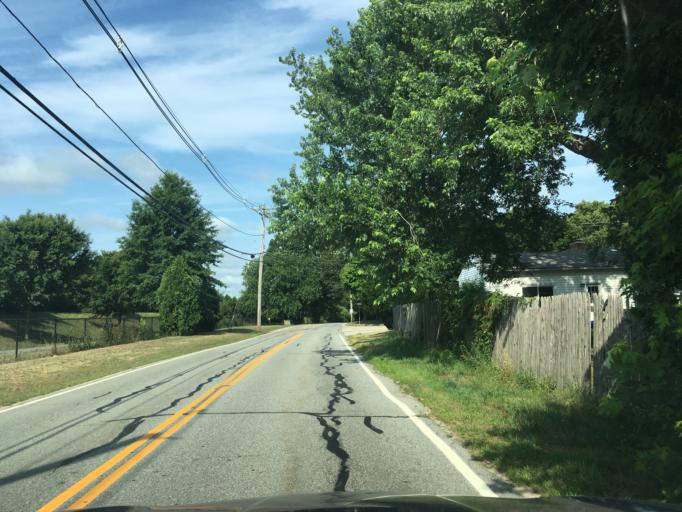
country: US
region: Rhode Island
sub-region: Kent County
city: East Greenwich
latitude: 41.6094
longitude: -71.4378
